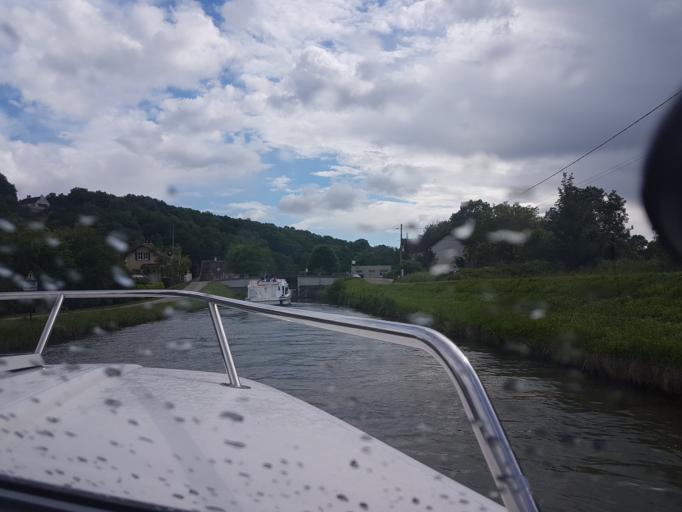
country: FR
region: Bourgogne
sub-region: Departement de la Nievre
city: Clamecy
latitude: 47.5341
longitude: 3.6318
